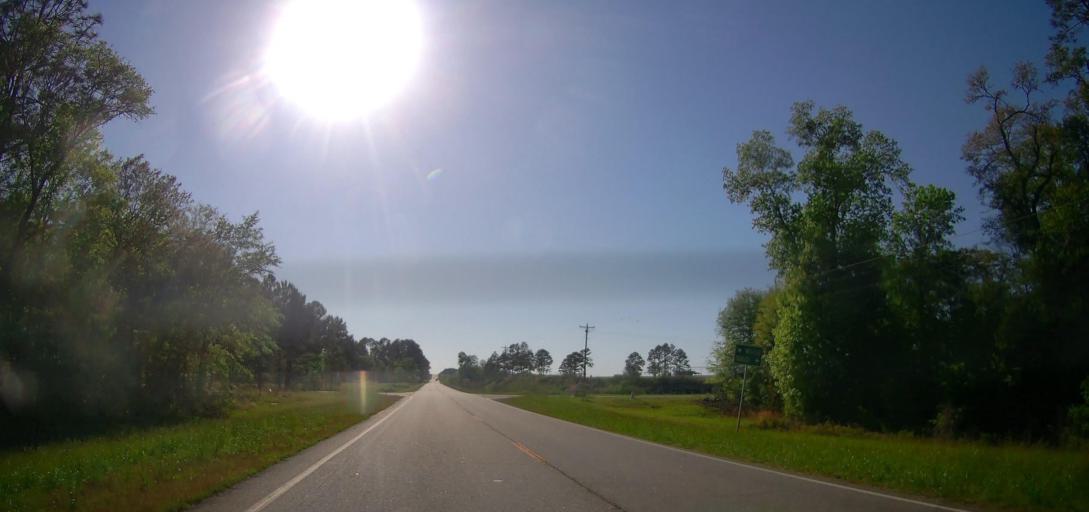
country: US
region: Georgia
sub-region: Turner County
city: Ashburn
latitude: 31.7207
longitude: -83.5054
